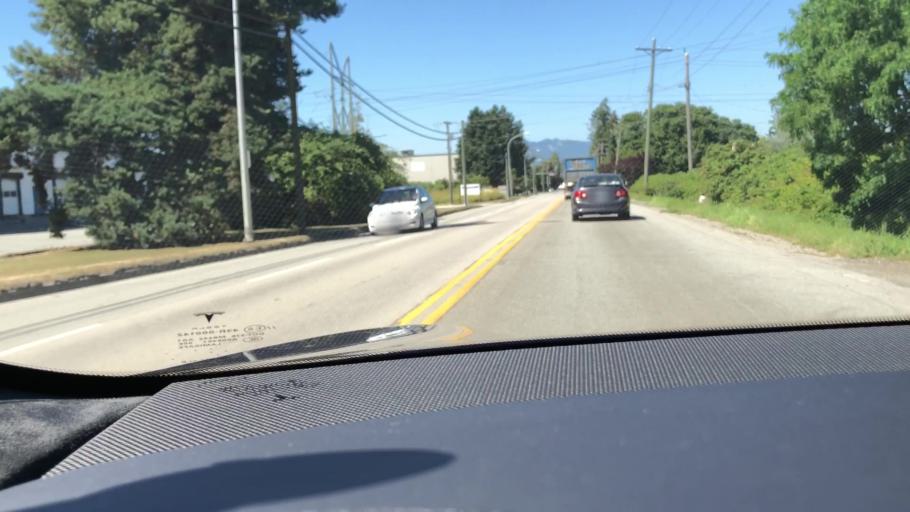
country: CA
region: British Columbia
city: Richmond
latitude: 49.1894
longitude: -123.0691
